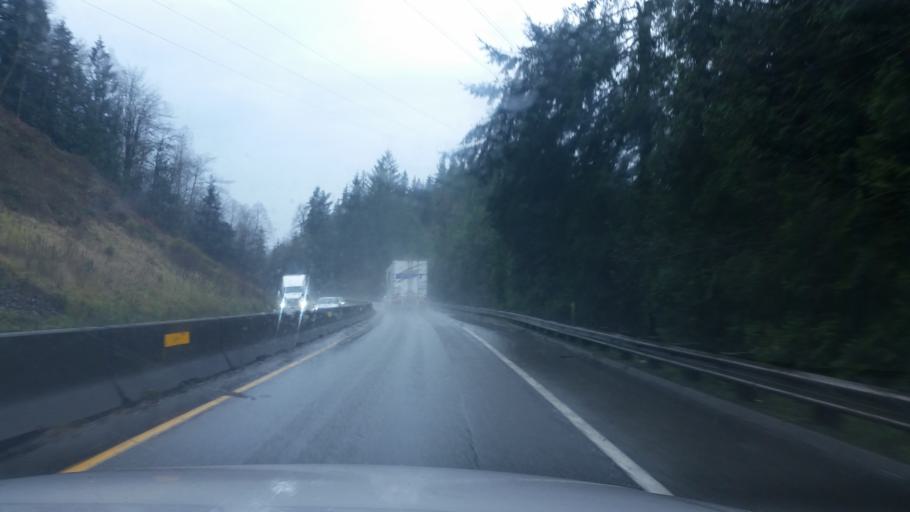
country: US
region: Washington
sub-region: King County
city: Hobart
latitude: 47.4580
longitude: -121.9495
